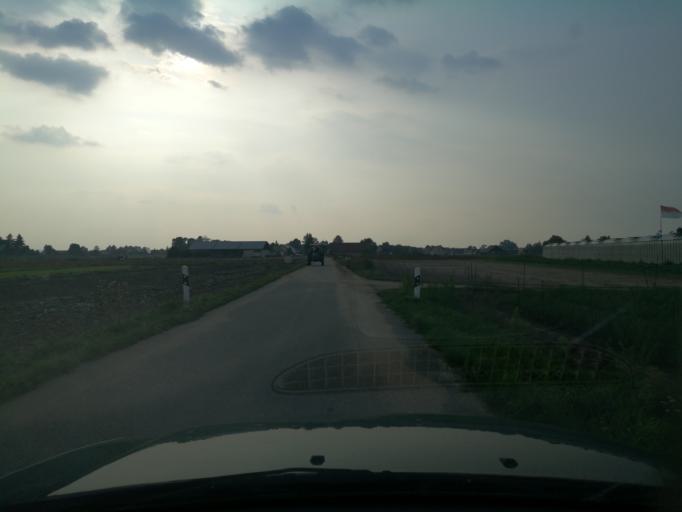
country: DE
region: Bavaria
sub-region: Regierungsbezirk Mittelfranken
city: Wetzendorf
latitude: 49.5196
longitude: 11.0609
